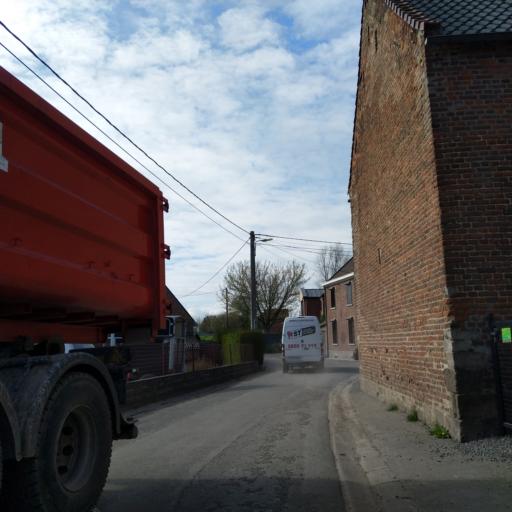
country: BE
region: Wallonia
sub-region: Province du Hainaut
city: Brugelette
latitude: 50.5879
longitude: 3.8799
